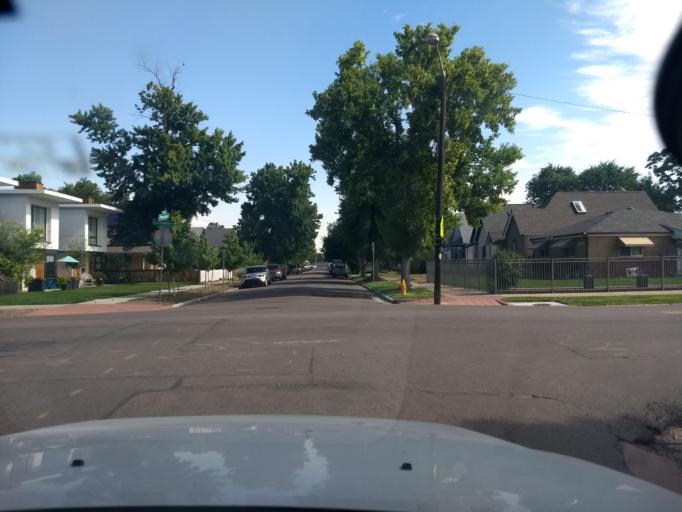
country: US
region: Colorado
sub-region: Arapahoe County
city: Englewood
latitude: 39.6929
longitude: -104.9816
